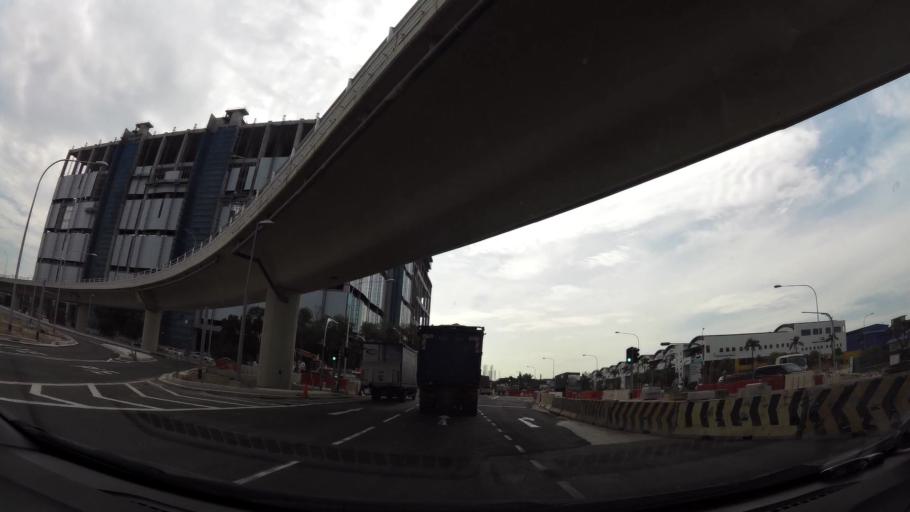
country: MY
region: Johor
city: Johor Bahru
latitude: 1.3150
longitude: 103.6556
